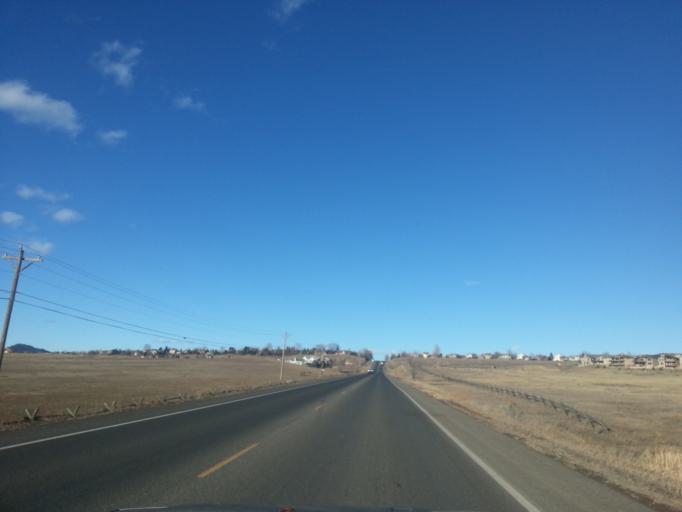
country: US
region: Colorado
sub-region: Larimer County
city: Fort Collins
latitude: 40.5184
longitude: -105.1151
